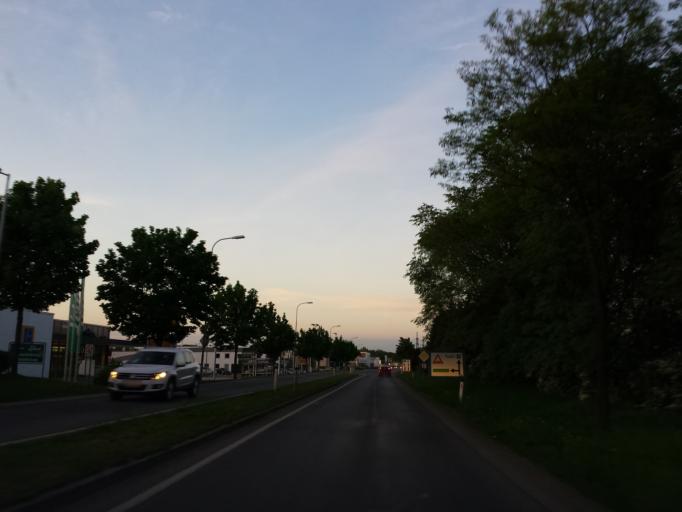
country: AT
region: Lower Austria
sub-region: Politischer Bezirk Tulln
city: Langenrohr
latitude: 48.3191
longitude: 16.0215
